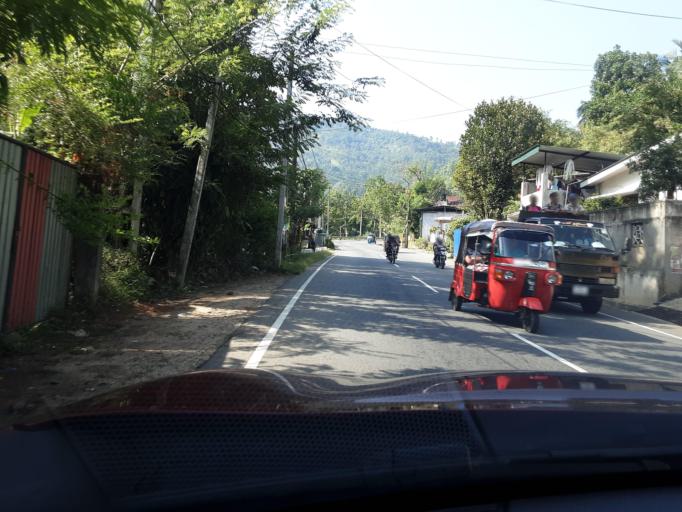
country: LK
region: Uva
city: Badulla
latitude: 6.9727
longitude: 81.0861
